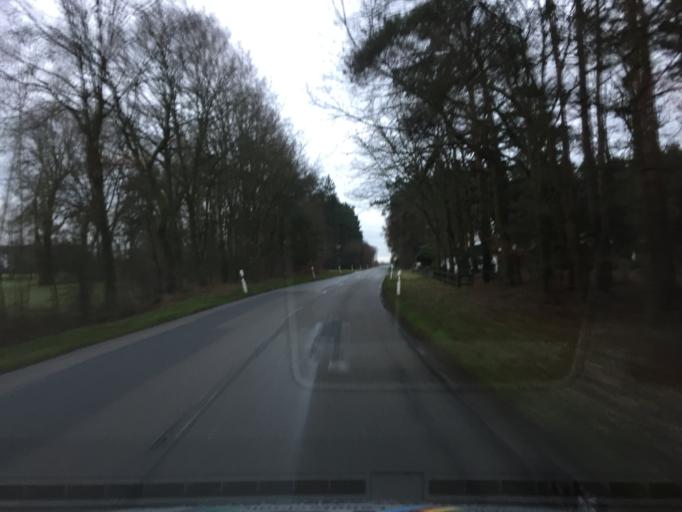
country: DE
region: Lower Saxony
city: Pennigsehl
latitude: 52.6449
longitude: 9.0012
